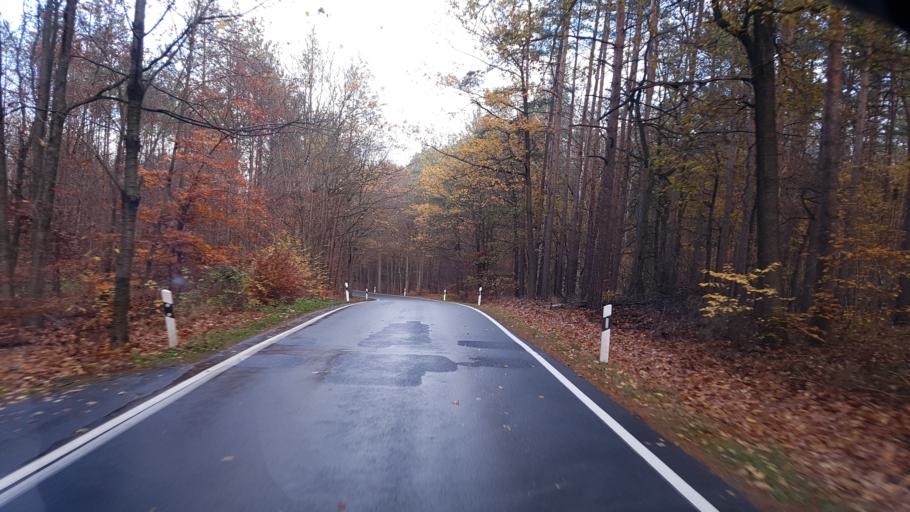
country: DE
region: Saxony
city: Thiendorf
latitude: 51.3306
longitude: 13.7545
